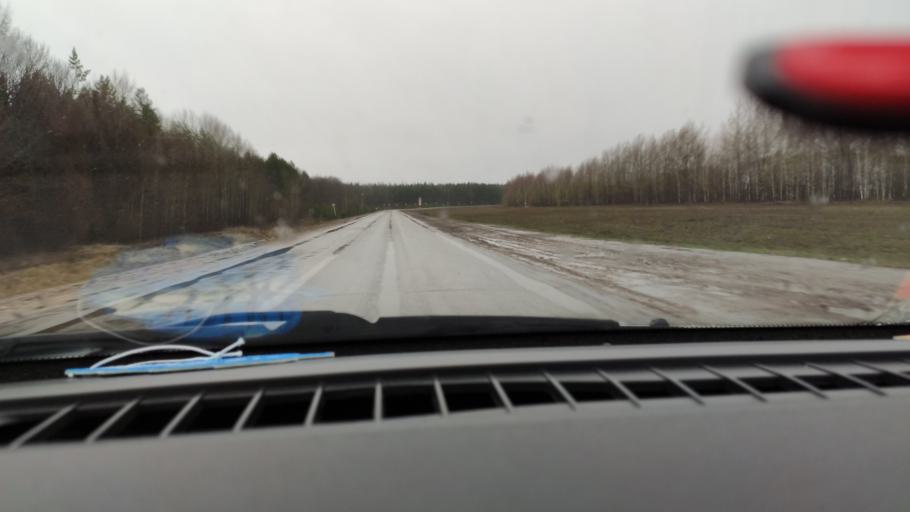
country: RU
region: Samara
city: Chelno-Vershiny
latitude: 54.6728
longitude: 51.0242
